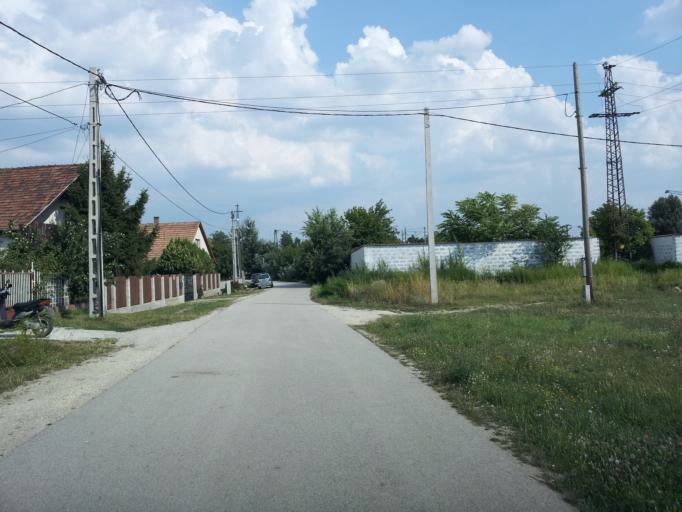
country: HU
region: Pest
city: Toekoel
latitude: 47.3219
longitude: 18.9820
